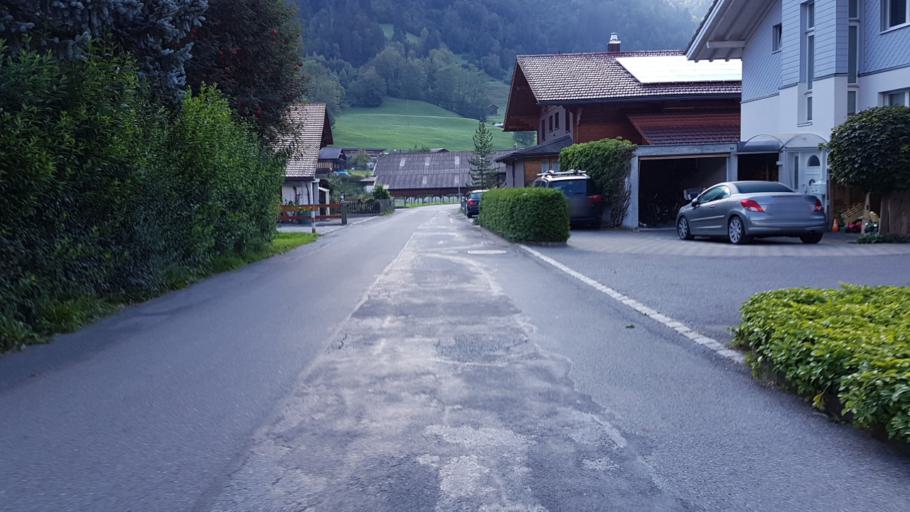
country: CH
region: Bern
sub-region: Frutigen-Niedersimmental District
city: Frutigen
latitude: 46.5836
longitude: 7.6559
